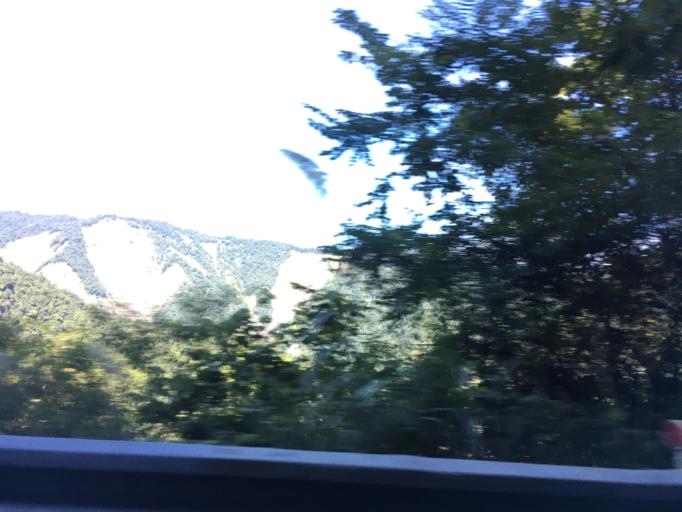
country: TW
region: Taiwan
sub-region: Yilan
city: Yilan
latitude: 24.5420
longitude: 121.5105
